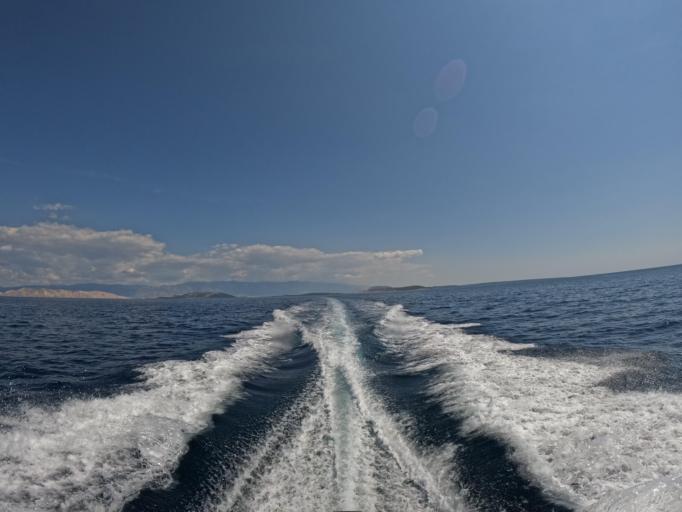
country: HR
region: Primorsko-Goranska
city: Lopar
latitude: 44.8892
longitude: 14.6357
